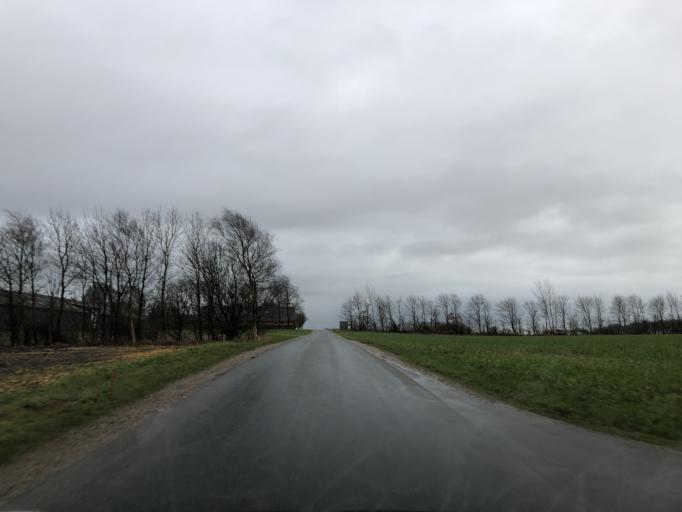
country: DK
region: Central Jutland
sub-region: Holstebro Kommune
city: Holstebro
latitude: 56.3778
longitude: 8.7276
